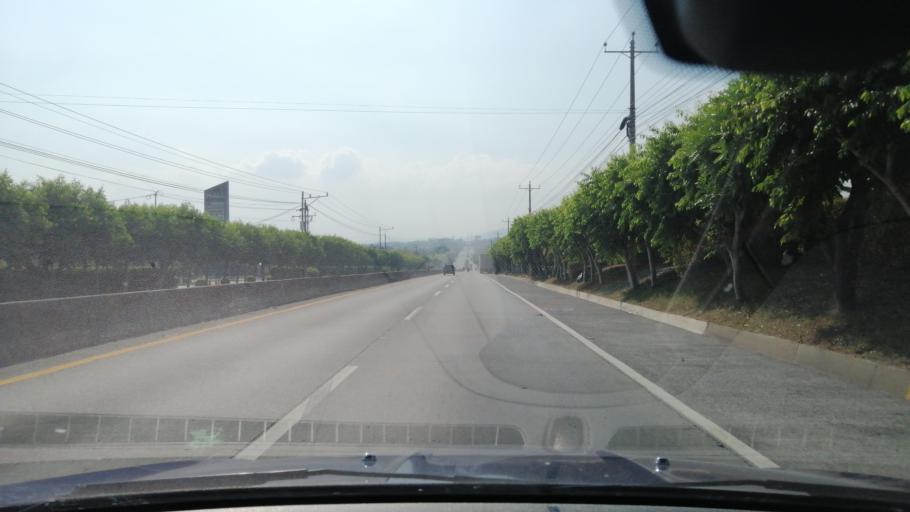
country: SV
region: San Salvador
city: Apopa
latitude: 13.7954
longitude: -89.2270
